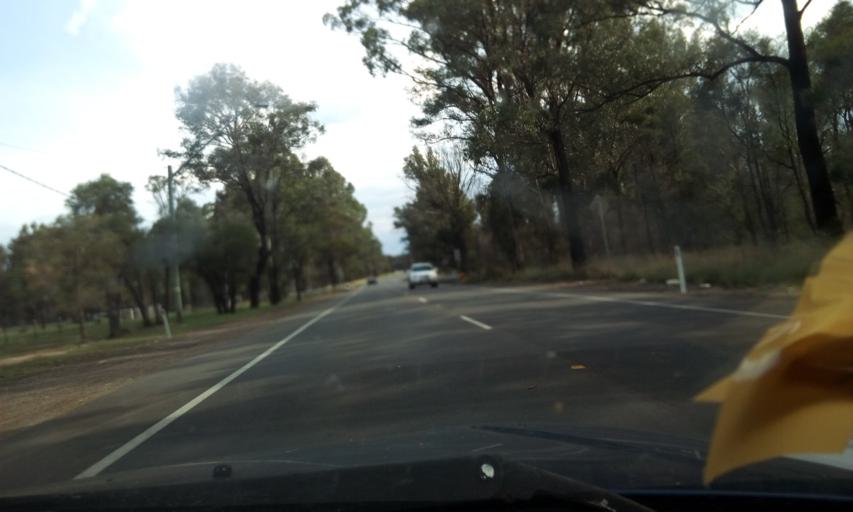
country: AU
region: New South Wales
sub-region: Penrith Municipality
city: Werrington Downs
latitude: -33.6988
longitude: 150.7269
